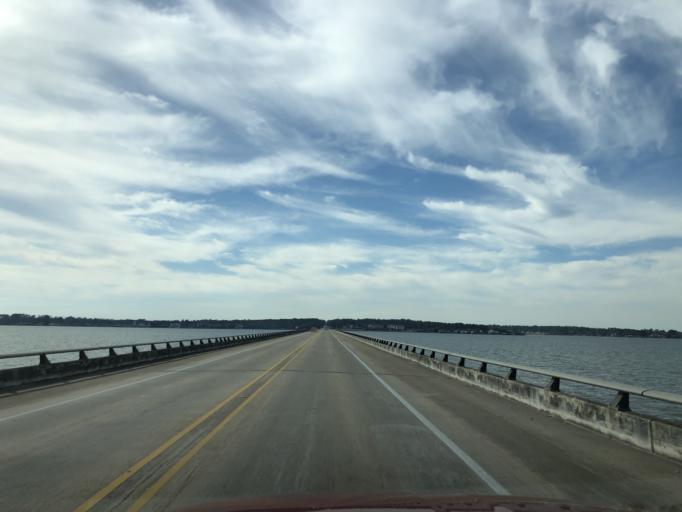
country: US
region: Texas
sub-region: Montgomery County
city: Willis
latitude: 30.4370
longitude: -95.5940
